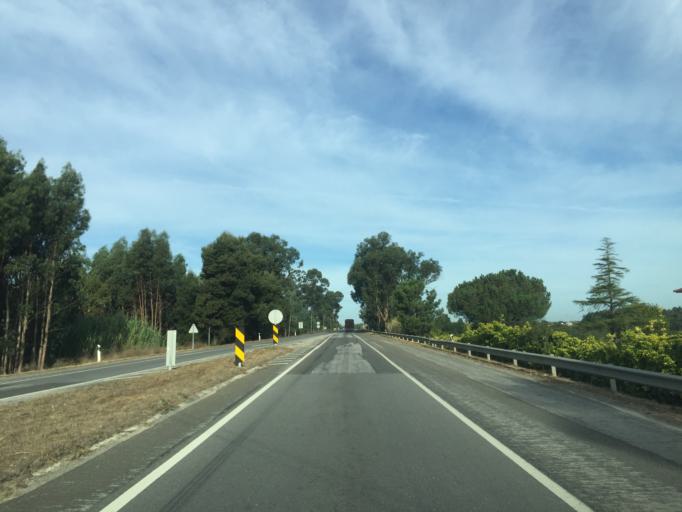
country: PT
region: Coimbra
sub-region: Figueira da Foz
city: Lavos
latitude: 40.0194
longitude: -8.8146
